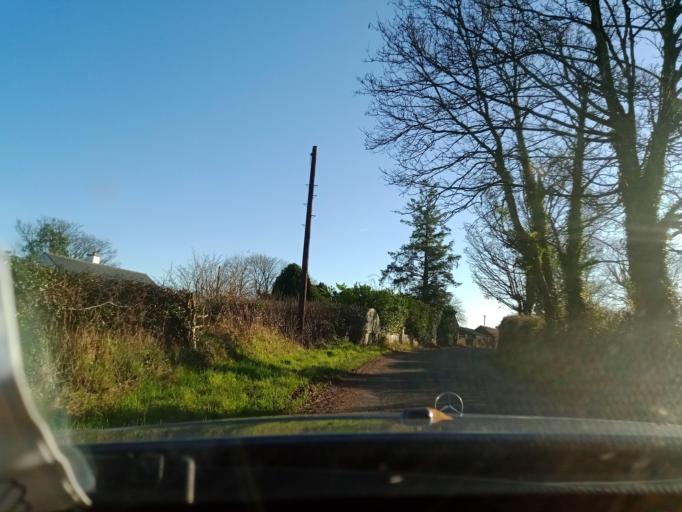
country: IE
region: Leinster
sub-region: Kilkenny
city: Mooncoin
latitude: 52.3051
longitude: -7.2252
